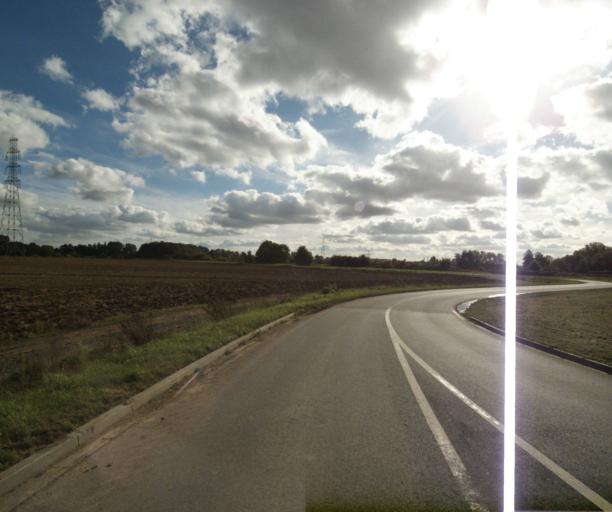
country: FR
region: Nord-Pas-de-Calais
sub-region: Departement du Nord
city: Bois-Grenier
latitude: 50.6621
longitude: 2.9024
